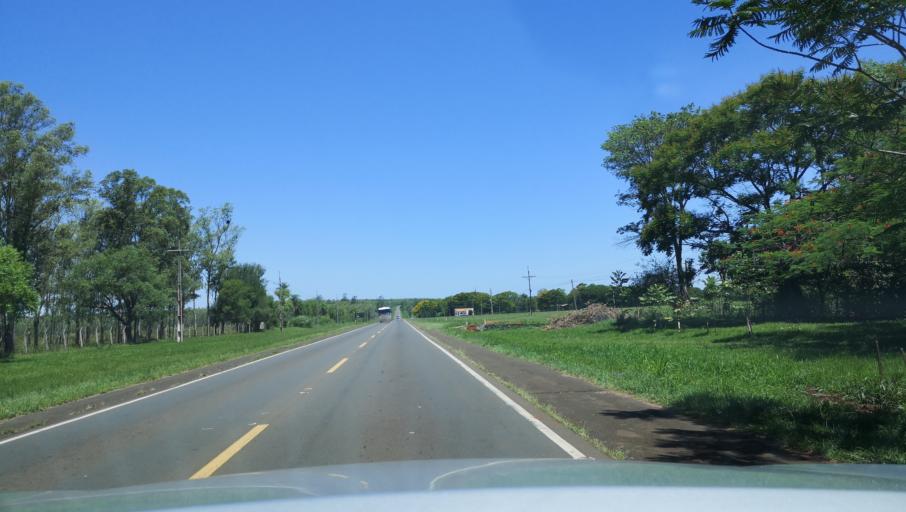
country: PY
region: Misiones
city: Santa Maria
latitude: -26.7422
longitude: -57.0463
